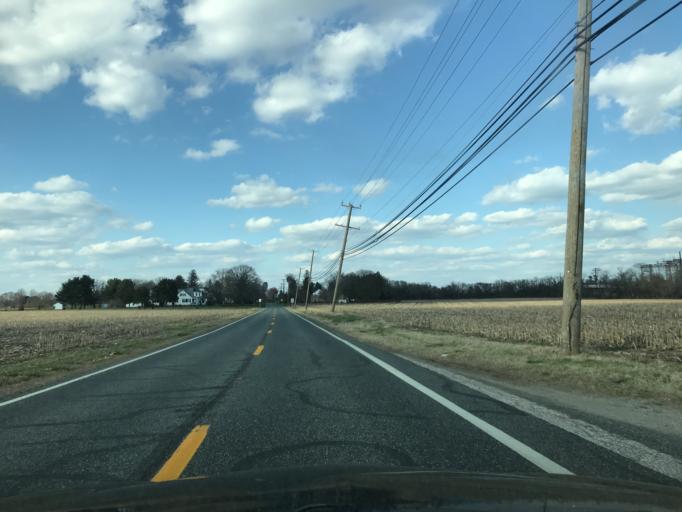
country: US
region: Maryland
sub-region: Harford County
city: Perryman
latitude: 39.4605
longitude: -76.2079
